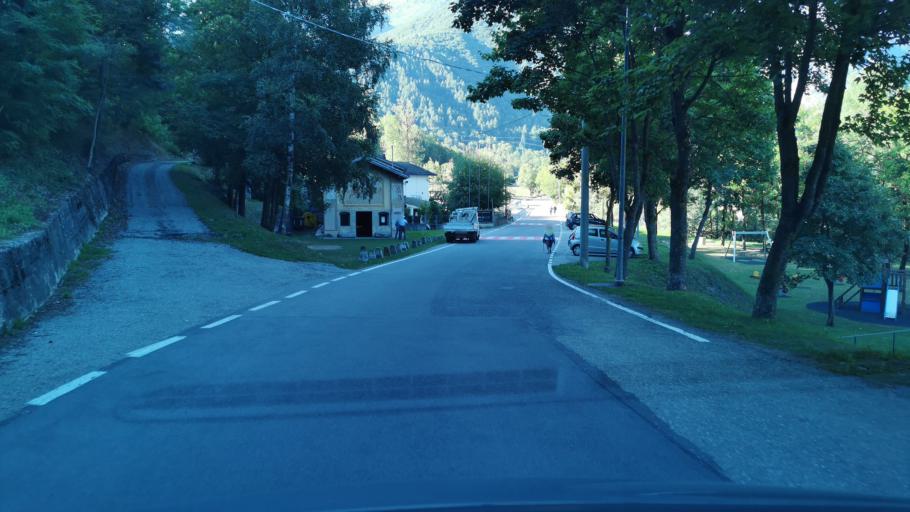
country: IT
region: Piedmont
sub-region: Provincia di Cuneo
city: Entracque
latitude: 44.2350
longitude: 7.3978
